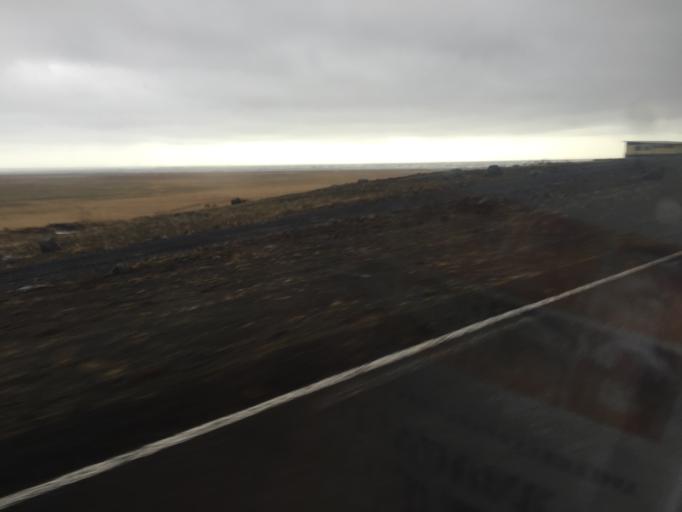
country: IS
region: East
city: Hoefn
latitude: 63.8789
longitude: -16.6624
